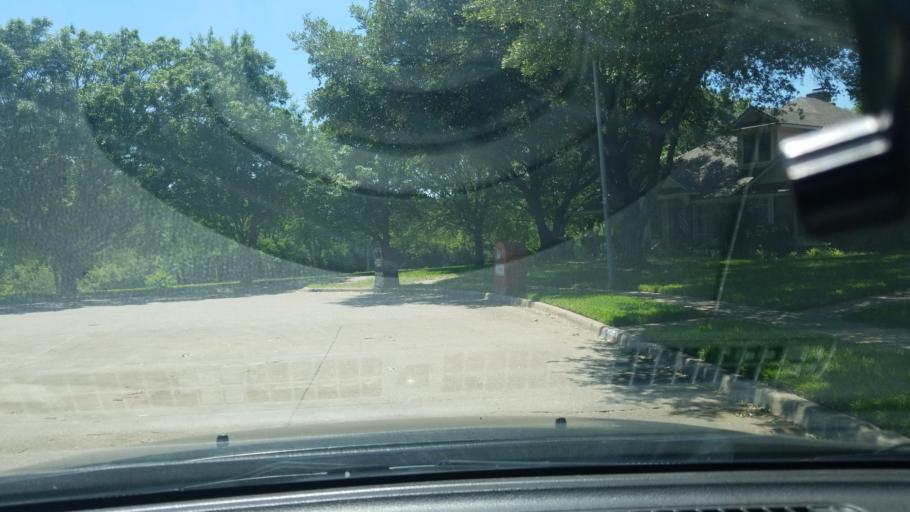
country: US
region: Texas
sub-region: Dallas County
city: Mesquite
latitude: 32.7599
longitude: -96.6106
